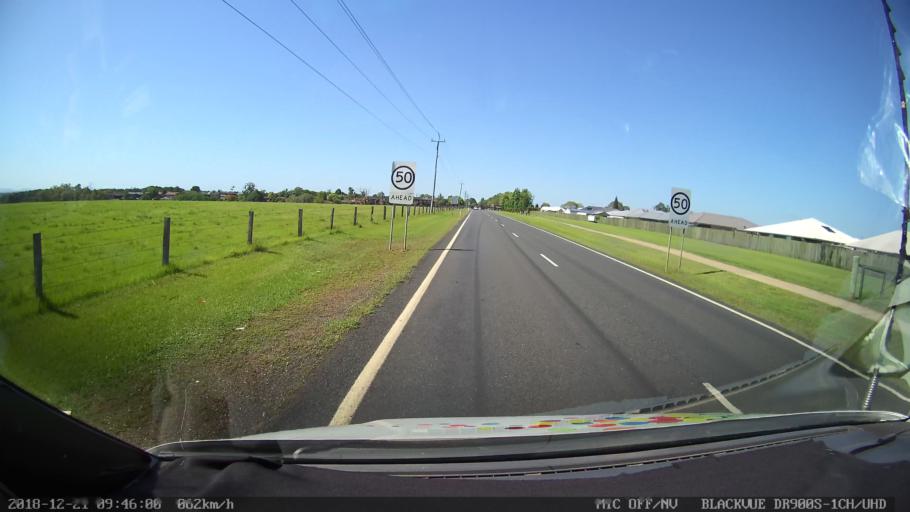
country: AU
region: New South Wales
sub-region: Clarence Valley
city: Grafton
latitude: -29.6350
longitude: 152.9273
